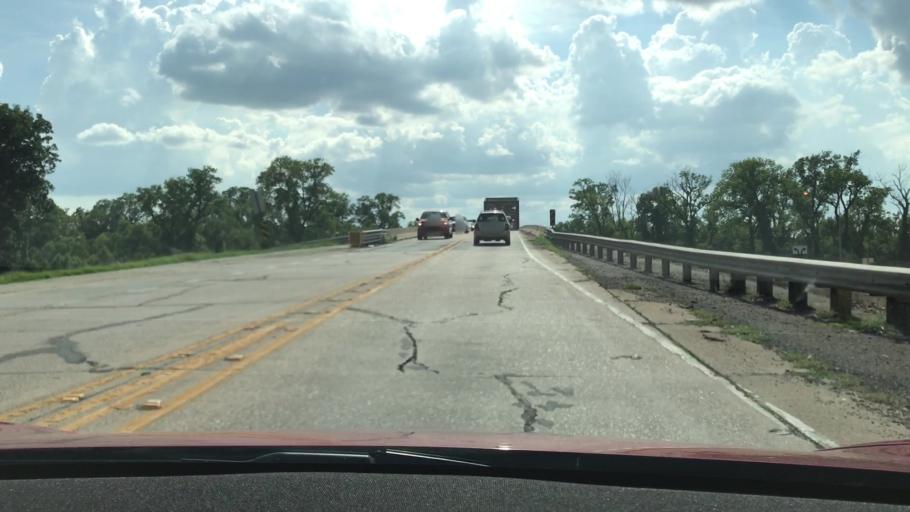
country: US
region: Louisiana
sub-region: Bossier Parish
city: Bossier City
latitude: 32.4589
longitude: -93.6738
